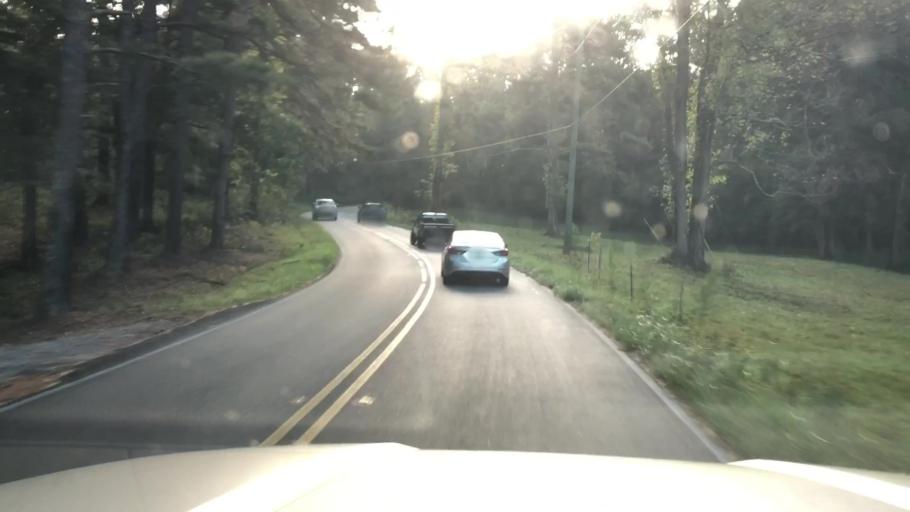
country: US
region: Georgia
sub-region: Bartow County
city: Emerson
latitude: 34.0817
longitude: -84.7362
